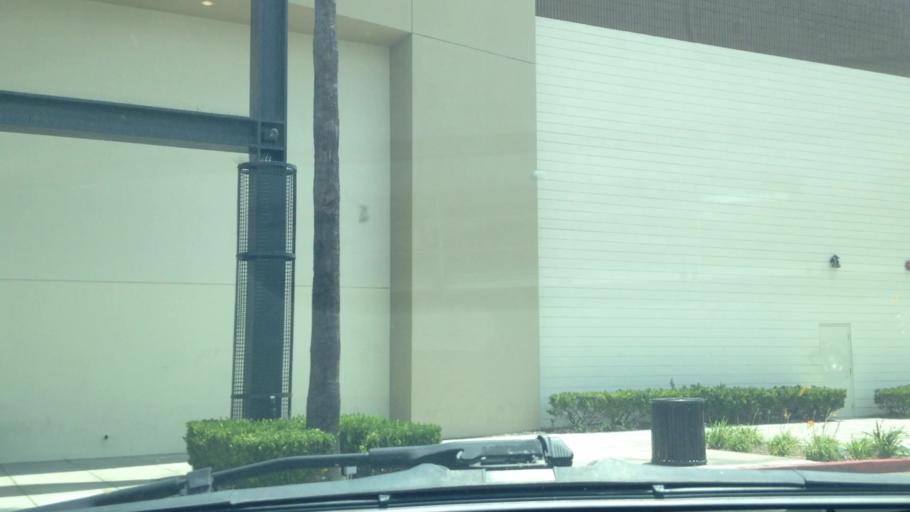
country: US
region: California
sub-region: Orange County
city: Anaheim
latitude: 33.8378
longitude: -117.9387
